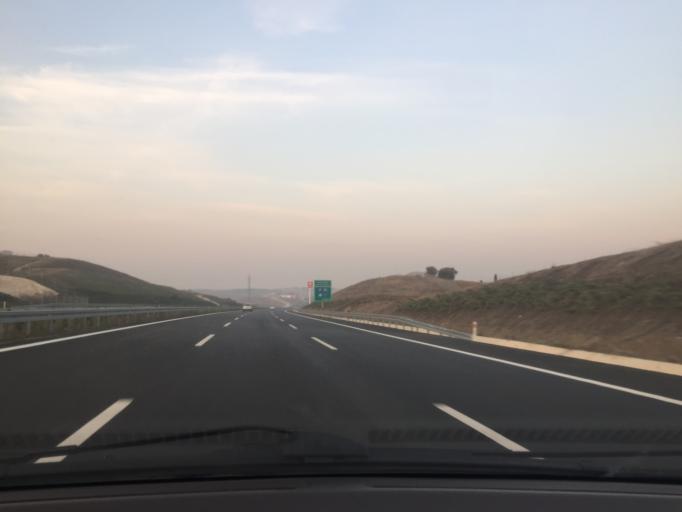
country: TR
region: Bursa
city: Karacabey
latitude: 40.2560
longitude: 28.4727
